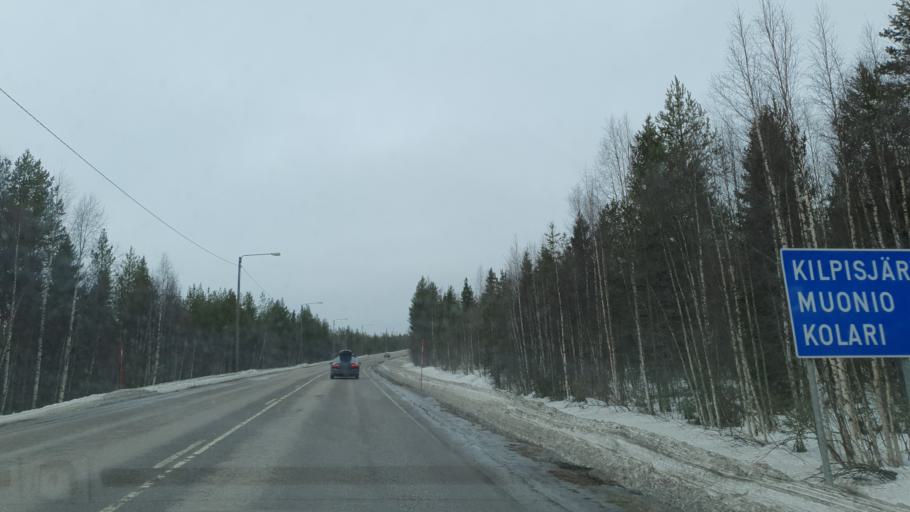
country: FI
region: Lapland
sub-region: Torniolaakso
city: Pello
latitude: 66.8265
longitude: 24.0022
